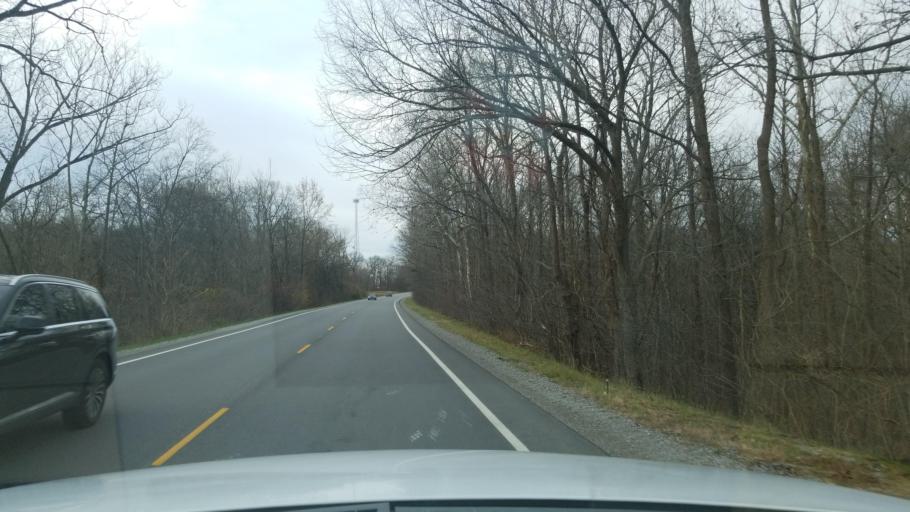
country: US
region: Illinois
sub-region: White County
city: Carmi
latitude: 37.9108
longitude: -88.1316
